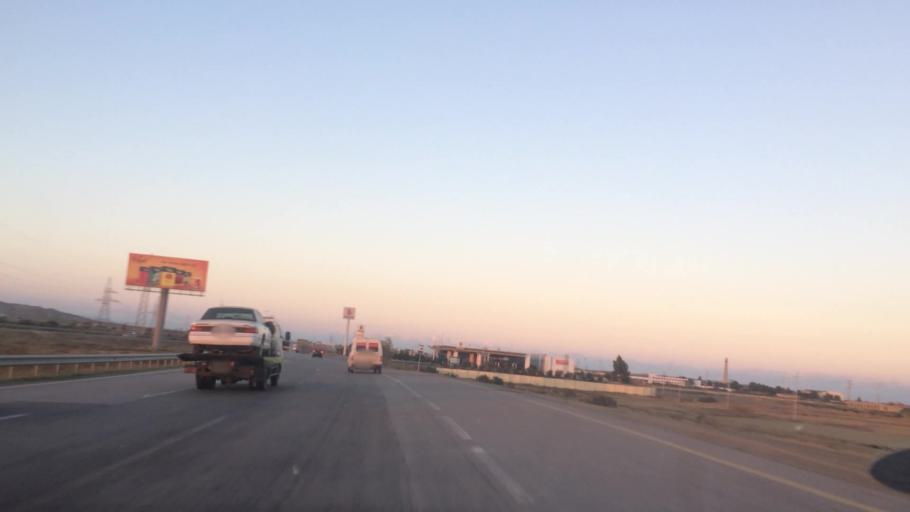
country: AZ
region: Baki
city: Qobustan
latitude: 39.9682
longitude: 49.4134
